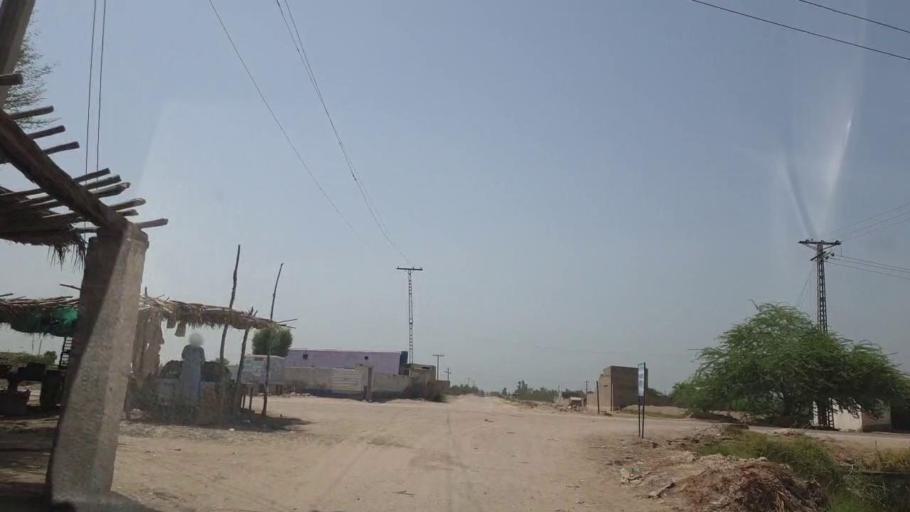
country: PK
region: Sindh
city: Ranipur
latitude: 27.2947
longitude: 68.5455
